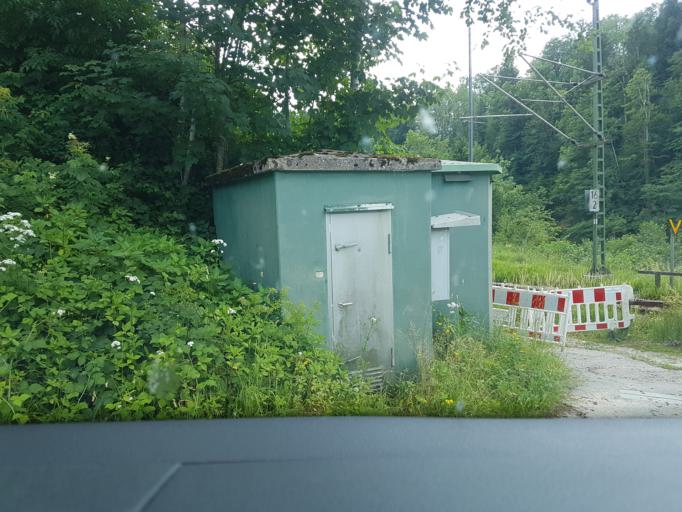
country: DE
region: Bavaria
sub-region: Upper Bavaria
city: Bischofswiesen
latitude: 47.6327
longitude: 12.9722
